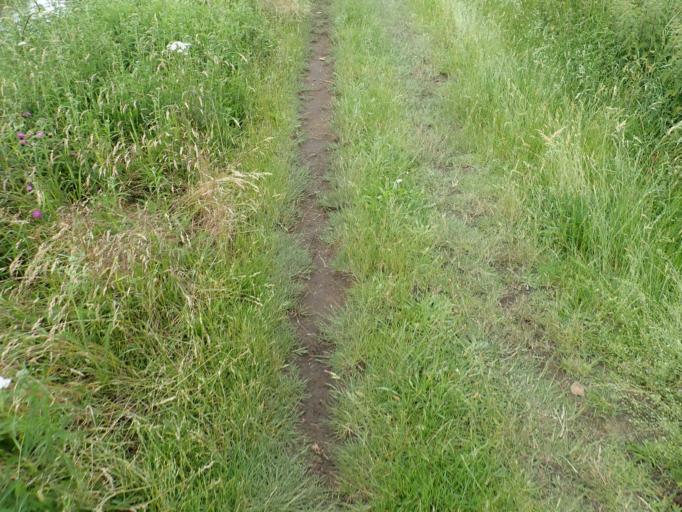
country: BE
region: Flanders
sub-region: Provincie Antwerpen
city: Heist-op-den-Berg
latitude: 51.1042
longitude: 4.7374
